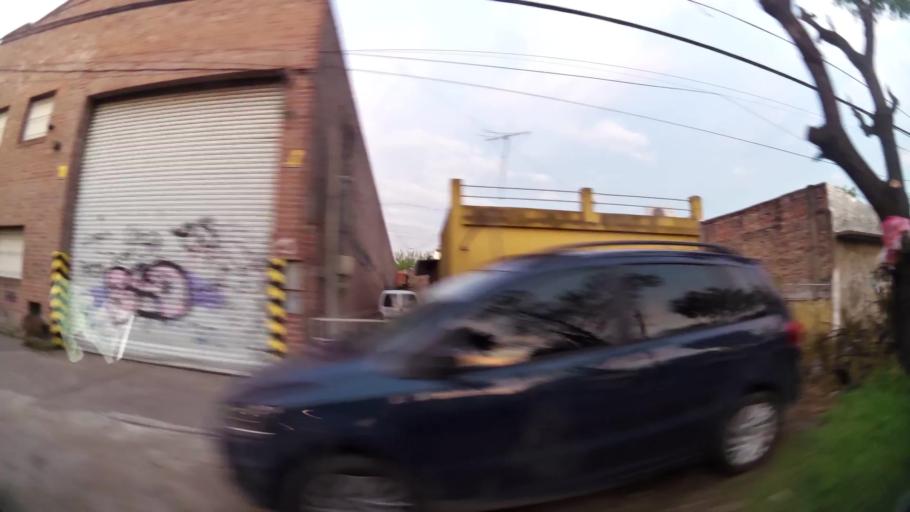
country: AR
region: Buenos Aires
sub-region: Partido de Lomas de Zamora
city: Lomas de Zamora
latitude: -34.7500
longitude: -58.3633
